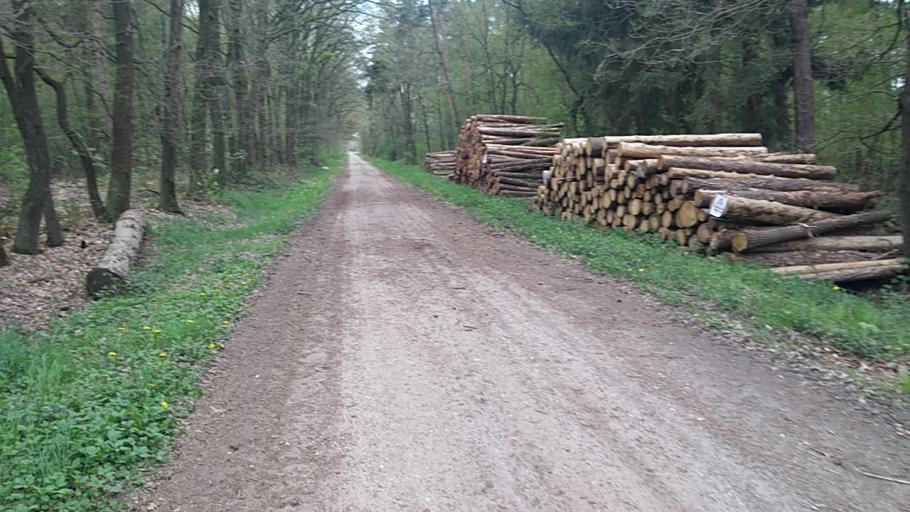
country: NL
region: Limburg
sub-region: Gemeente Leudal
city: Heythuysen
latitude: 51.2918
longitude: 5.8808
